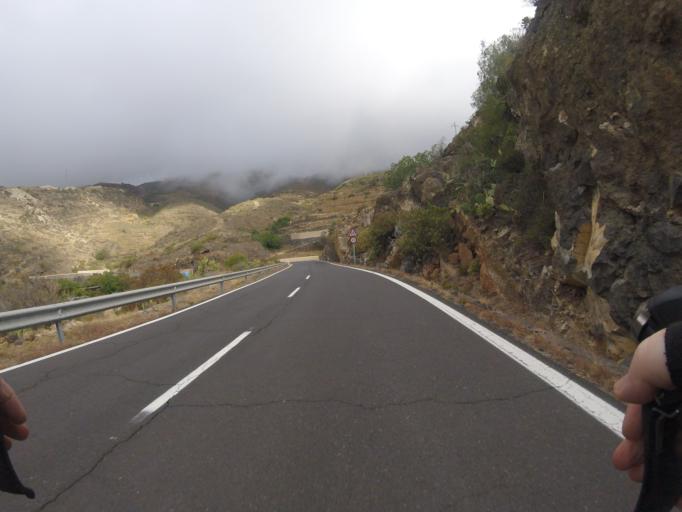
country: ES
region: Canary Islands
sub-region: Provincia de Santa Cruz de Tenerife
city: Fasnia
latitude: 28.2278
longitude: -16.4466
